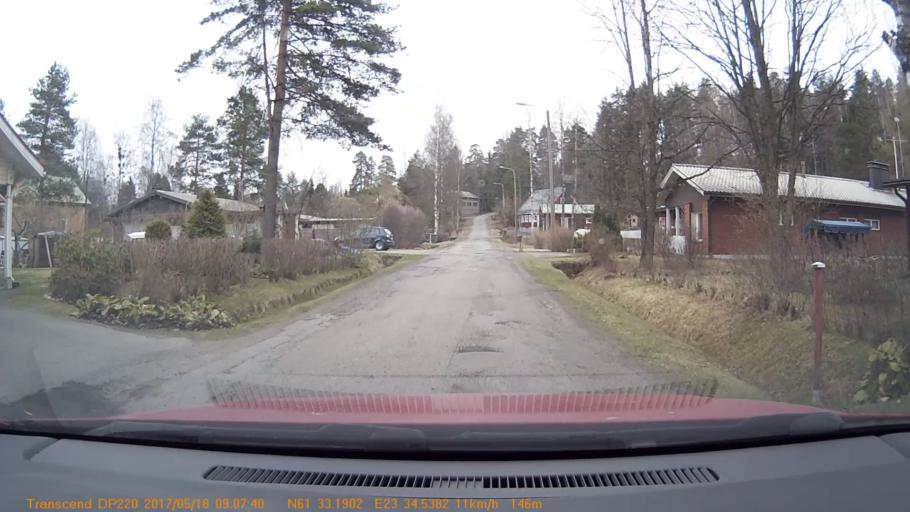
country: FI
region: Pirkanmaa
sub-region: Tampere
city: Yloejaervi
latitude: 61.5529
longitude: 23.5761
